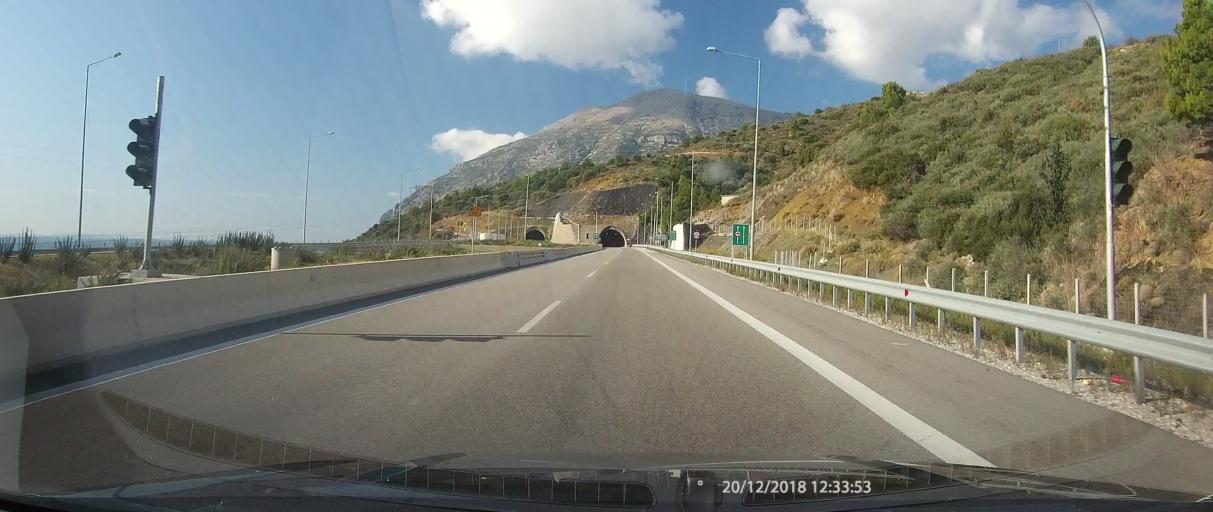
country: GR
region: West Greece
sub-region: Nomos Aitolias kai Akarnanias
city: Antirrio
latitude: 38.3527
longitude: 21.7292
